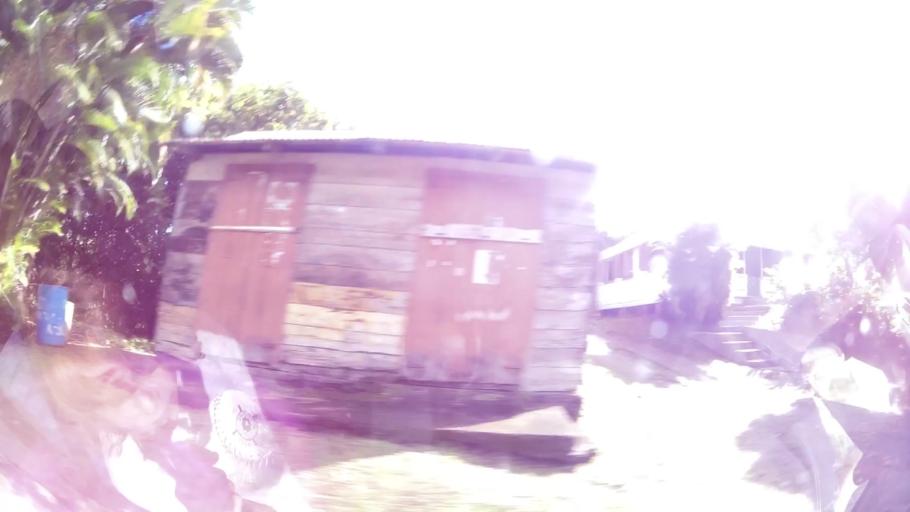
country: DM
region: Saint Andrew
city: Marigot
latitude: 15.5129
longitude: -61.2629
